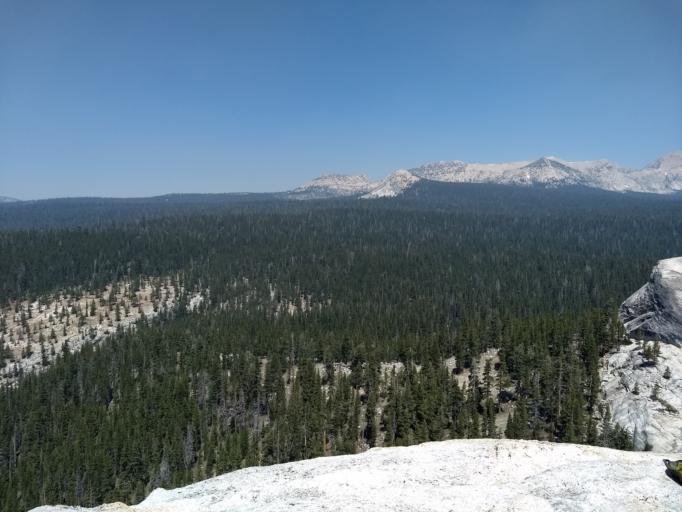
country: US
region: California
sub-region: Mariposa County
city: Yosemite Valley
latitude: 37.8819
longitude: -119.3470
